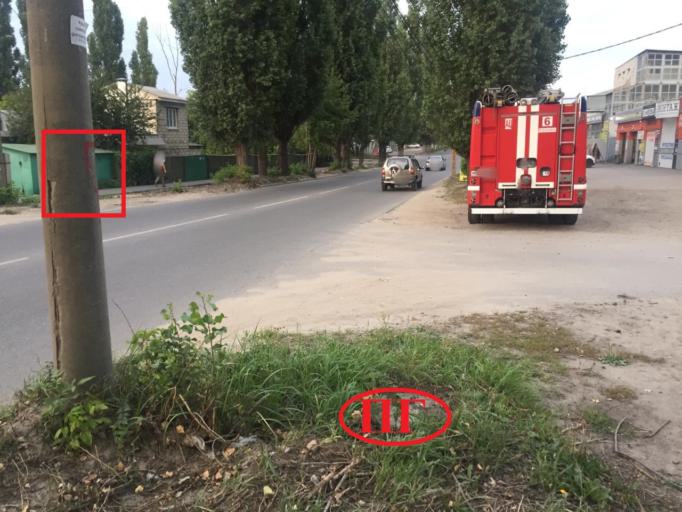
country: RU
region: Voronezj
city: Voronezh
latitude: 51.6803
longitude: 39.1616
